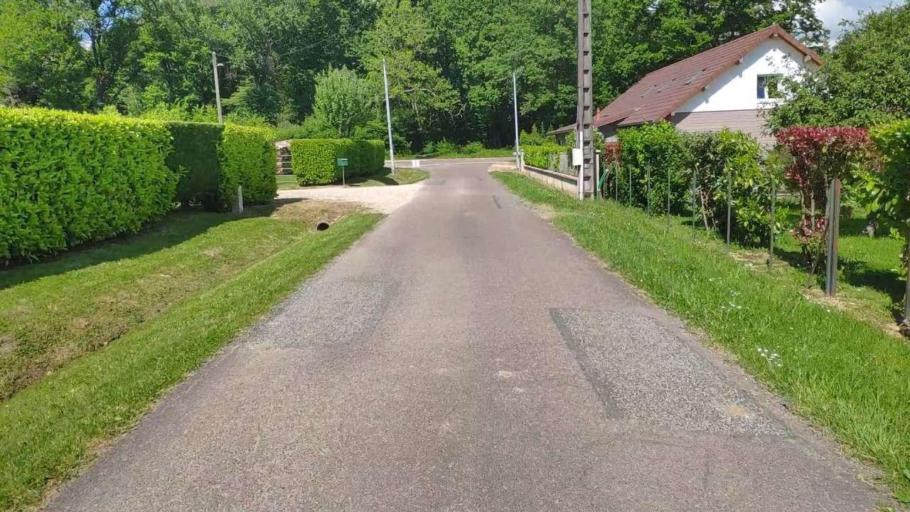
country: FR
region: Franche-Comte
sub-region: Departement du Jura
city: Bletterans
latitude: 46.8044
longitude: 5.4286
